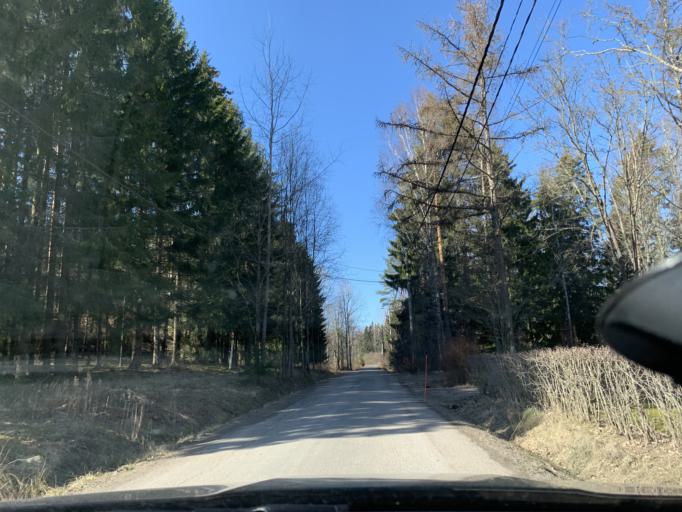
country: FI
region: Uusimaa
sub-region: Helsinki
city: Espoo
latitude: 60.1700
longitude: 24.5897
